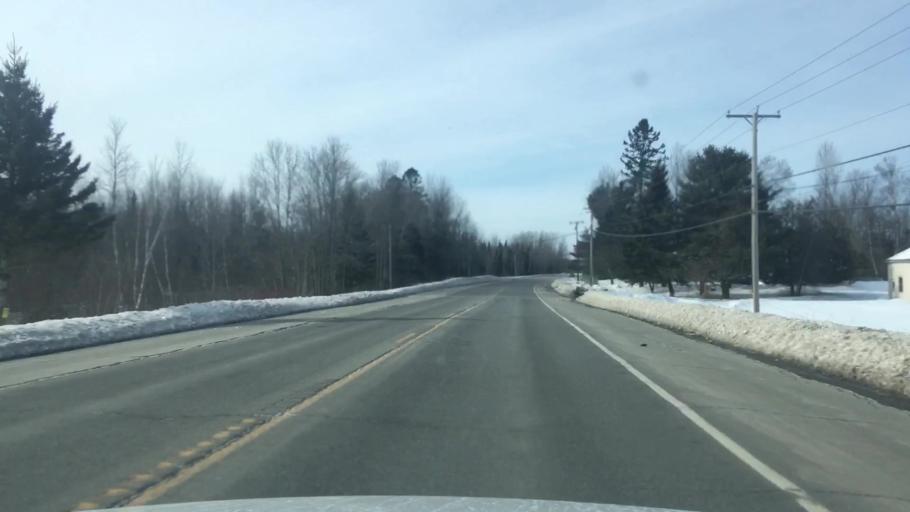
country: US
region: Maine
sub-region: Penobscot County
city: Kenduskeag
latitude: 44.9063
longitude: -68.8924
